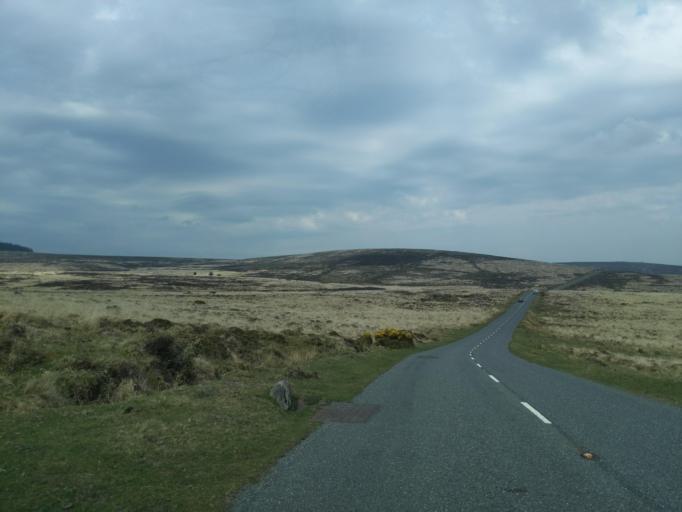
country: GB
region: England
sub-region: Devon
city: Ashburton
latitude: 50.6066
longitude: -3.8904
